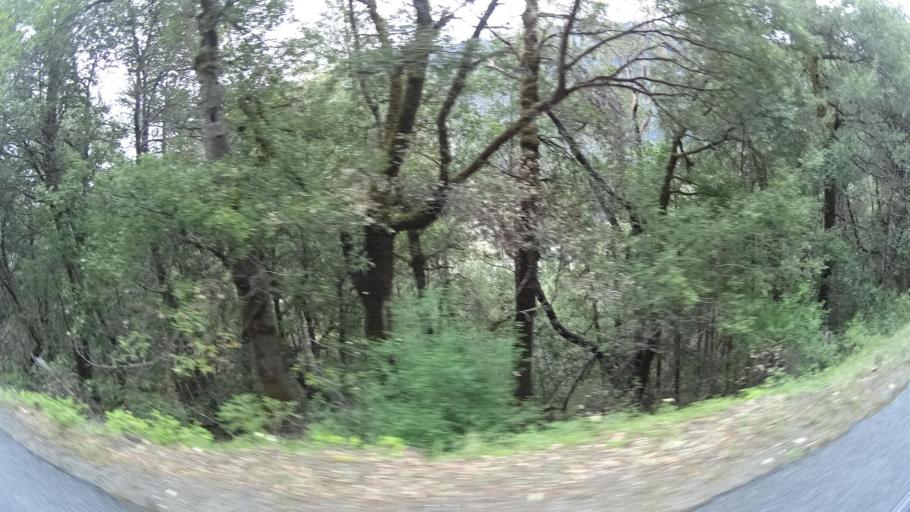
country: US
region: California
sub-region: Humboldt County
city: Willow Creek
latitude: 41.3523
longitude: -123.5117
